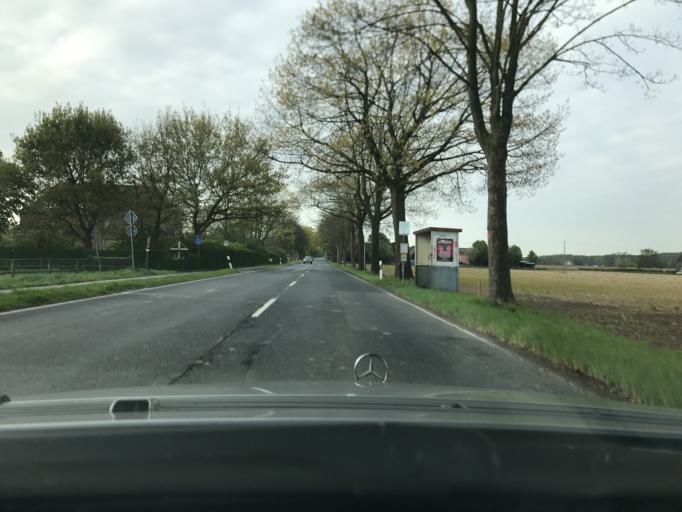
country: DE
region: North Rhine-Westphalia
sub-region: Regierungsbezirk Dusseldorf
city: Krefeld
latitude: 51.3943
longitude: 6.5581
